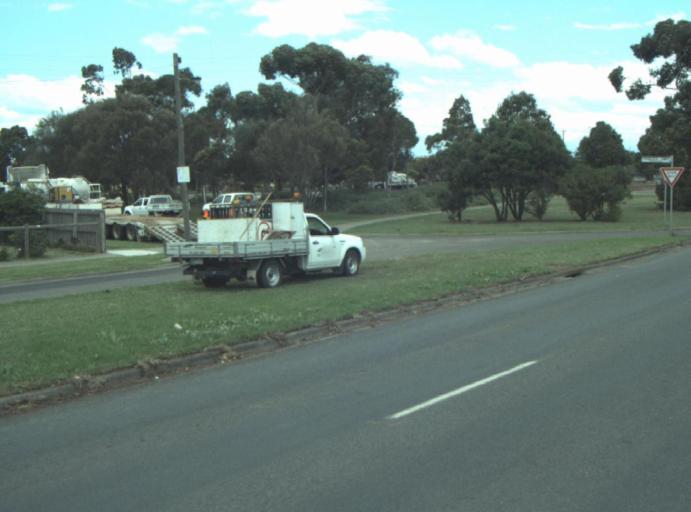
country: AU
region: Victoria
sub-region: Greater Geelong
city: Bell Park
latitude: -38.0824
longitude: 144.3582
